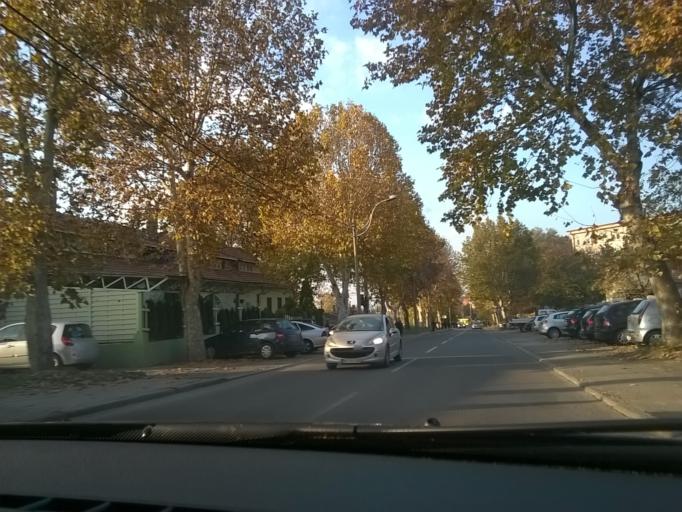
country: RS
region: Central Serbia
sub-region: Belgrade
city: Palilula
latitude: 44.8127
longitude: 20.4926
